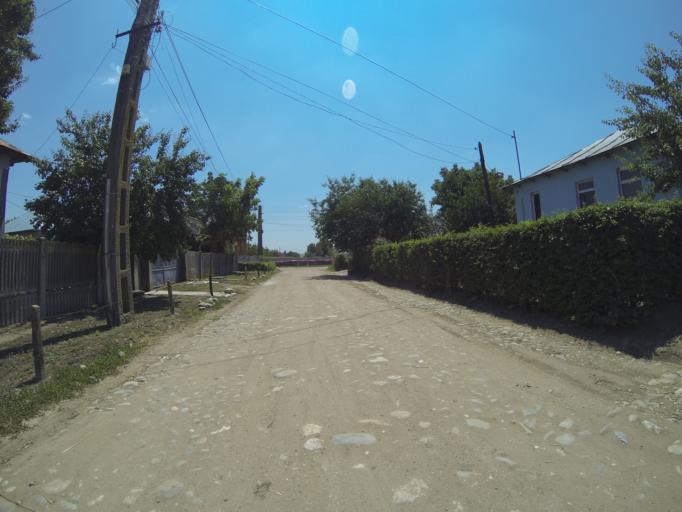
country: RO
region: Dolj
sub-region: Comuna Segarcea
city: Segarcea
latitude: 44.0876
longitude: 23.7486
